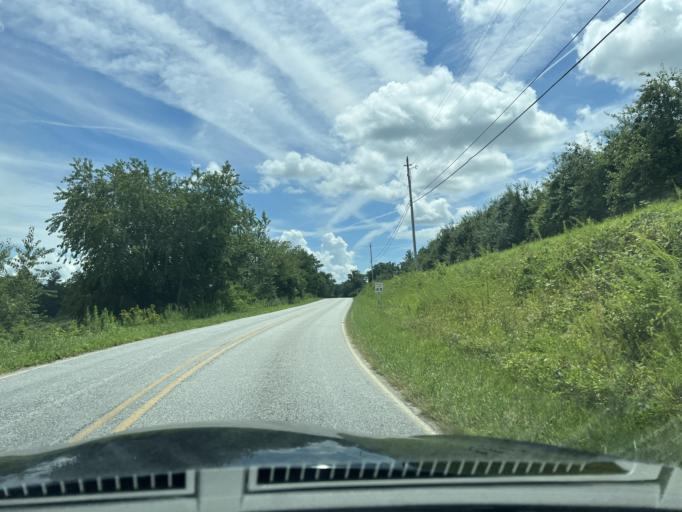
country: US
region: North Carolina
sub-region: Henderson County
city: Fruitland
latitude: 35.4067
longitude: -82.3900
